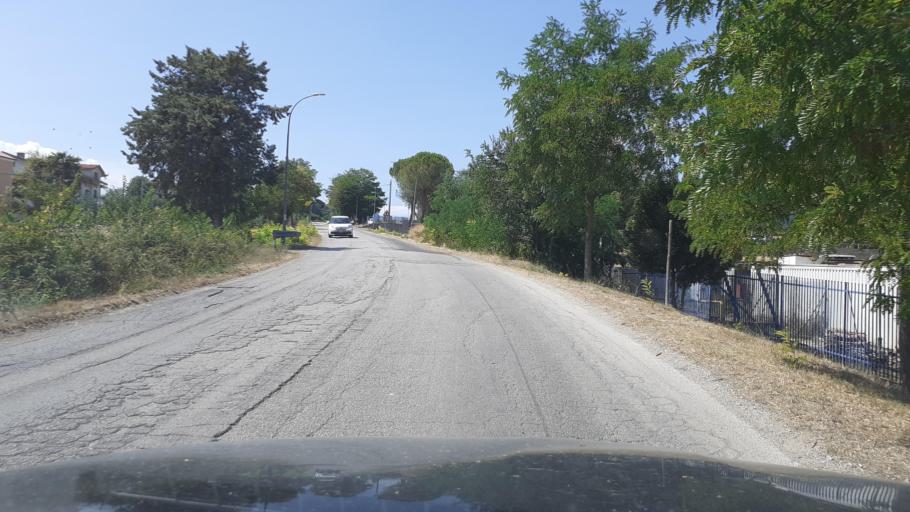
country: IT
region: Abruzzo
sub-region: Provincia di Chieti
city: Santa Maria Imbaro
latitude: 42.2151
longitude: 14.4571
